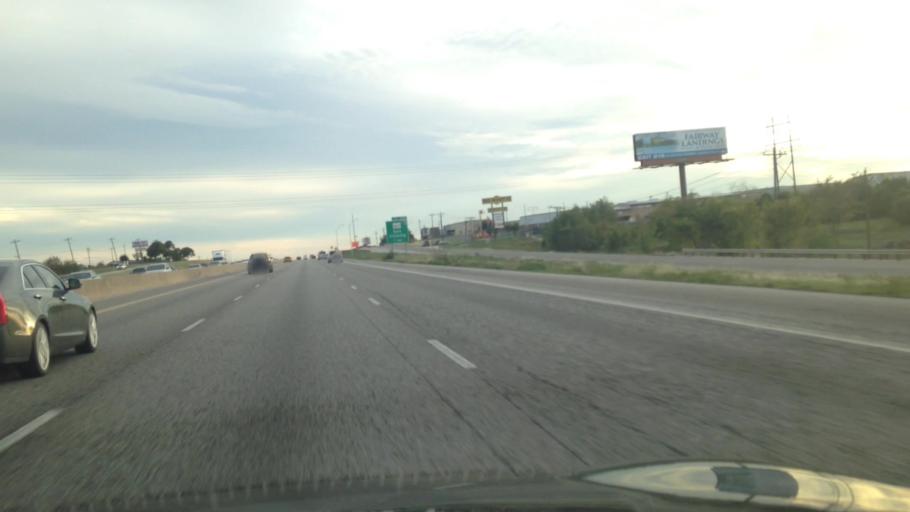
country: US
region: Texas
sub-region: Hays County
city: Buda
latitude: 30.0718
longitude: -97.8278
